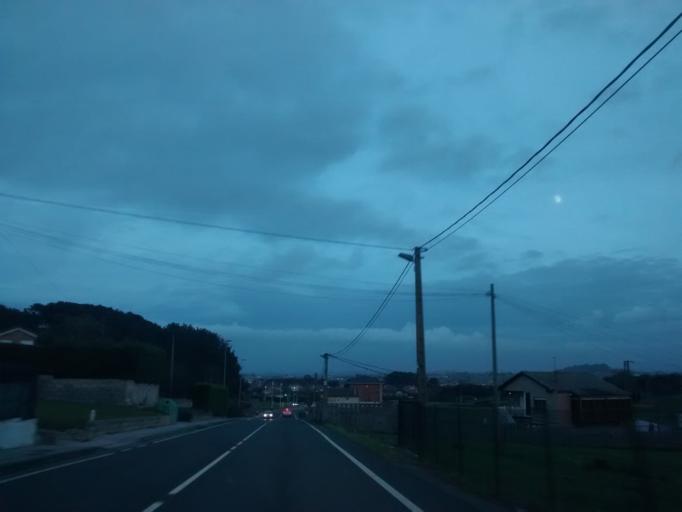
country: ES
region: Cantabria
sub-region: Provincia de Cantabria
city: Santa Cruz de Bezana
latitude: 43.4619
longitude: -3.9172
